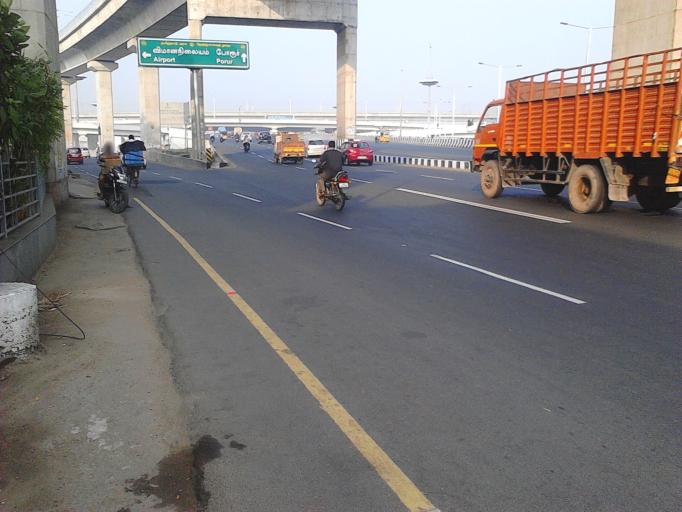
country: IN
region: Tamil Nadu
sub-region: Kancheepuram
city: Alandur
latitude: 13.0075
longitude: 80.2063
